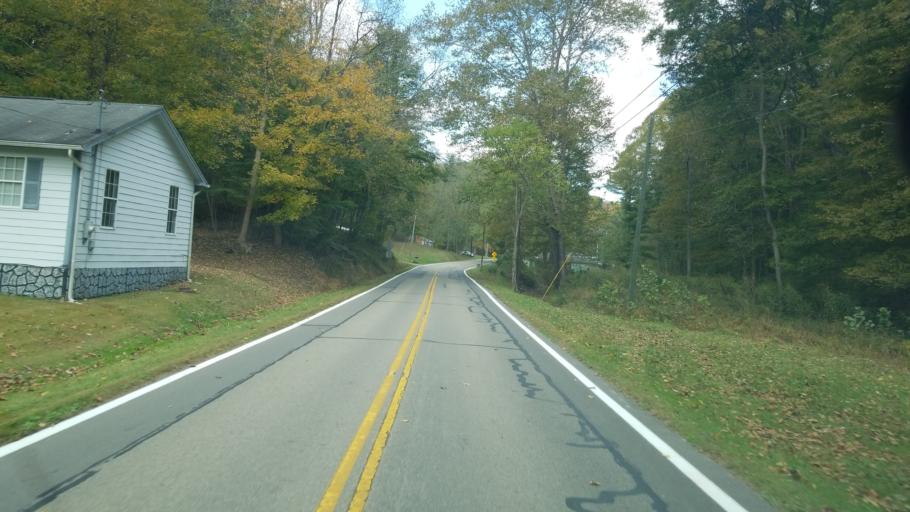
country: US
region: Ohio
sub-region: Jackson County
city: Jackson
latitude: 39.0758
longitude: -82.5996
